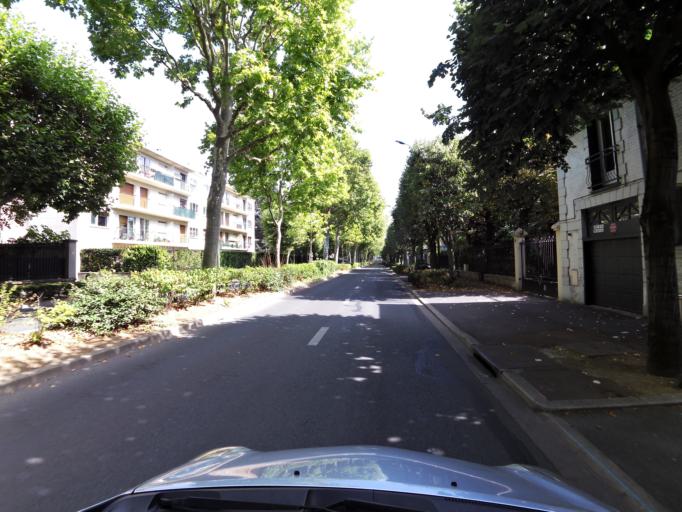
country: FR
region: Ile-de-France
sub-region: Departement du Val-de-Marne
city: Joinville-le-Pont
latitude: 48.8286
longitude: 2.4661
